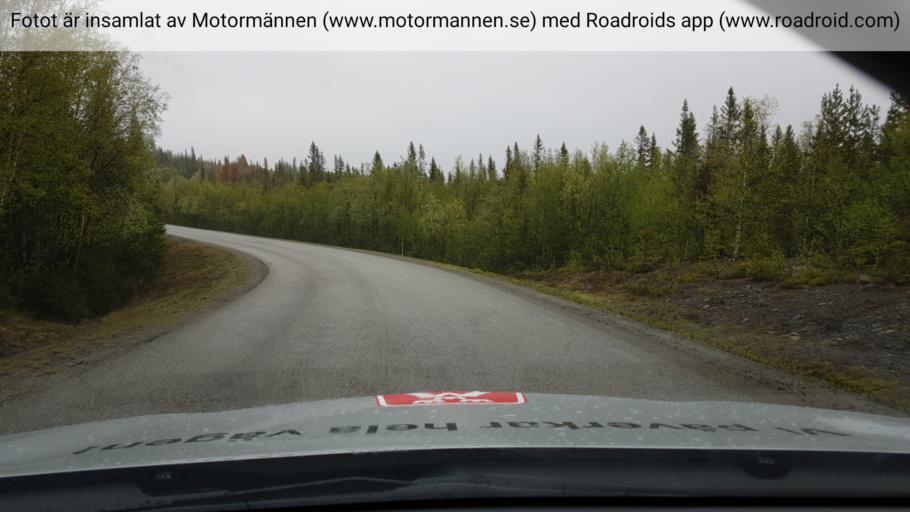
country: SE
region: Jaemtland
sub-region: Krokoms Kommun
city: Valla
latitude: 63.0288
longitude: 13.9495
